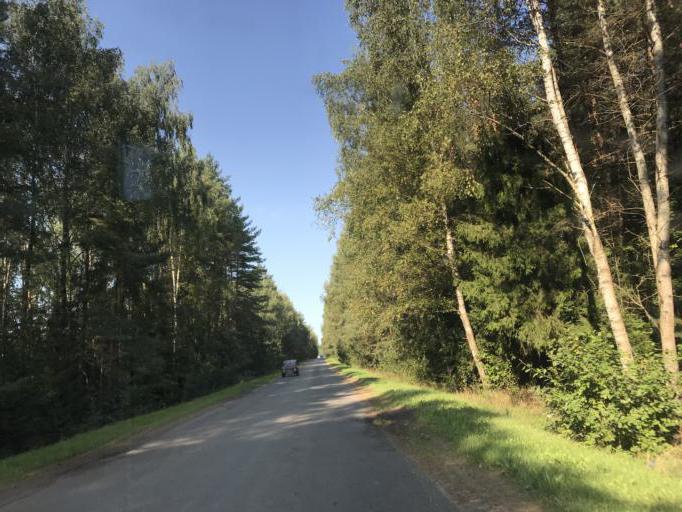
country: BY
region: Mogilev
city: Myazhysyatki
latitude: 53.8015
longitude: 30.1724
